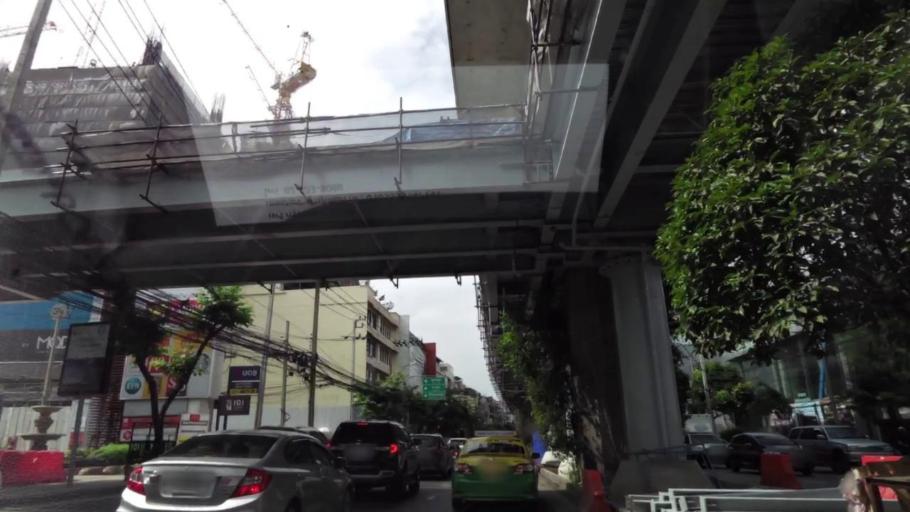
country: TH
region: Bangkok
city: Phra Khanong
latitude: 13.6864
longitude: 100.6103
